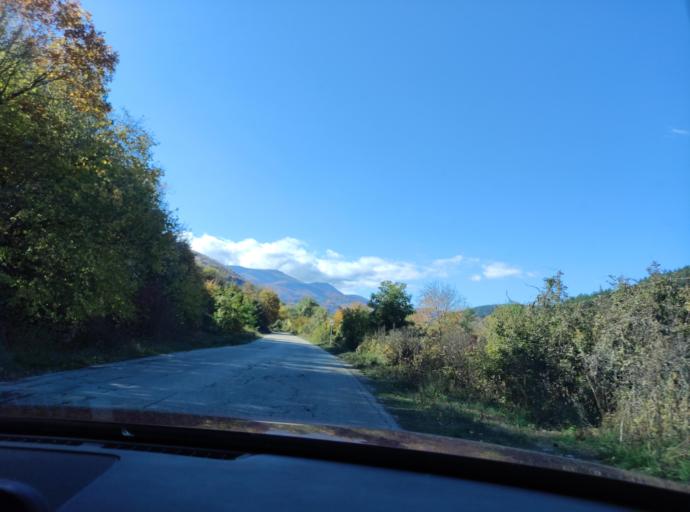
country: BG
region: Montana
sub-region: Obshtina Chiprovtsi
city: Chiprovtsi
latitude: 43.3808
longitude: 22.9056
